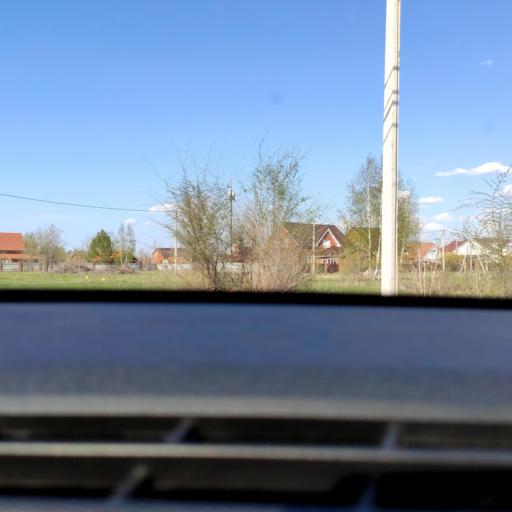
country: RU
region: Samara
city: Tol'yatti
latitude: 53.5567
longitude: 49.3819
